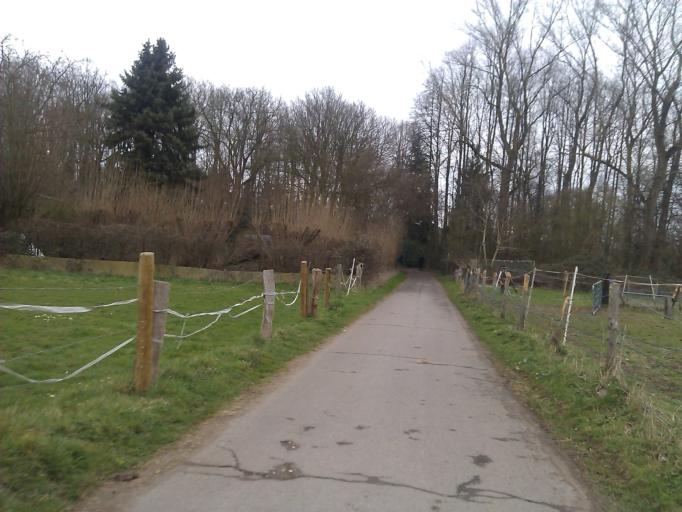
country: DE
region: North Rhine-Westphalia
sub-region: Regierungsbezirk Koln
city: Porz am Rhein
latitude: 50.8770
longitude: 7.0419
